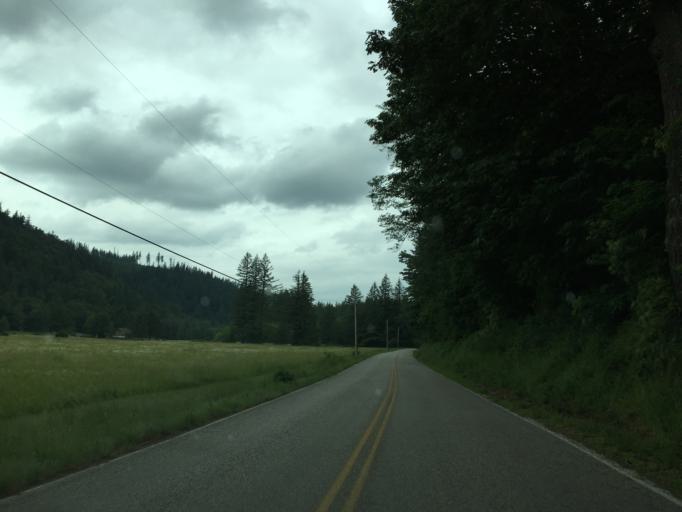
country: US
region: Washington
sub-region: Whatcom County
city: Peaceful Valley
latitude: 48.9694
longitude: -122.0768
